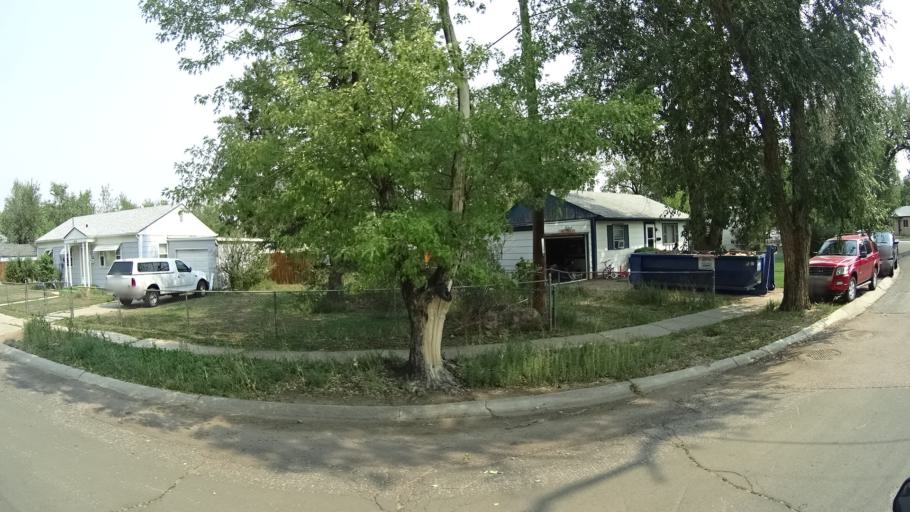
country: US
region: Colorado
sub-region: El Paso County
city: Colorado Springs
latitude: 38.8043
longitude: -104.8147
